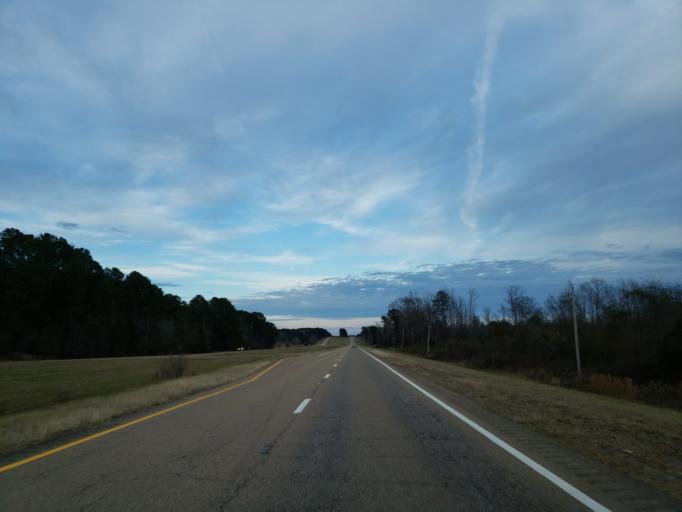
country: US
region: Mississippi
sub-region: Lauderdale County
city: Meridian Station
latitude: 32.5013
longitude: -88.5655
